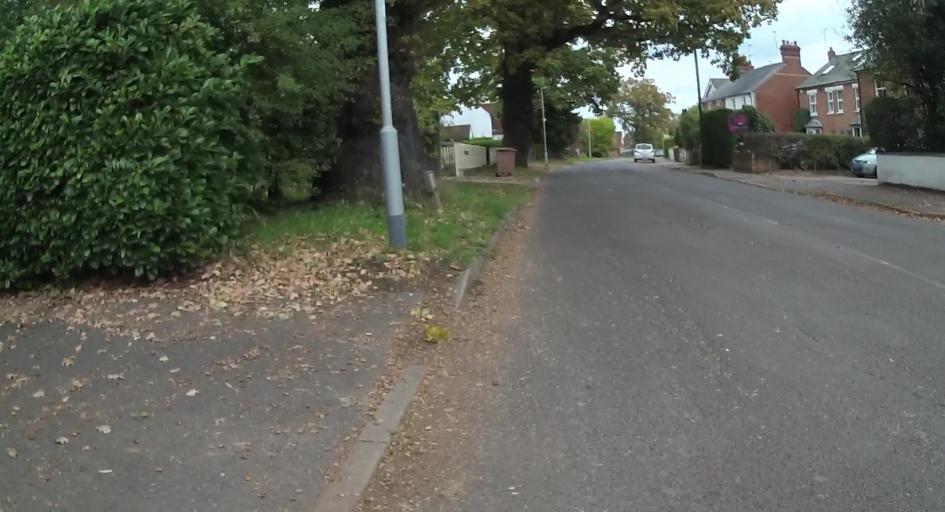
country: GB
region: England
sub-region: Wokingham
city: Wokingham
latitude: 51.3963
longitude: -0.8512
